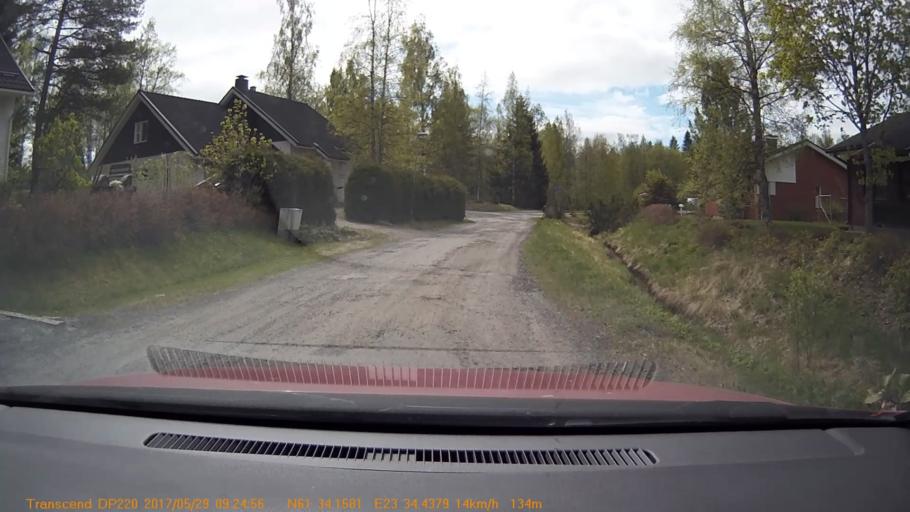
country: FI
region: Pirkanmaa
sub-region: Tampere
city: Yloejaervi
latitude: 61.5693
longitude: 23.5739
